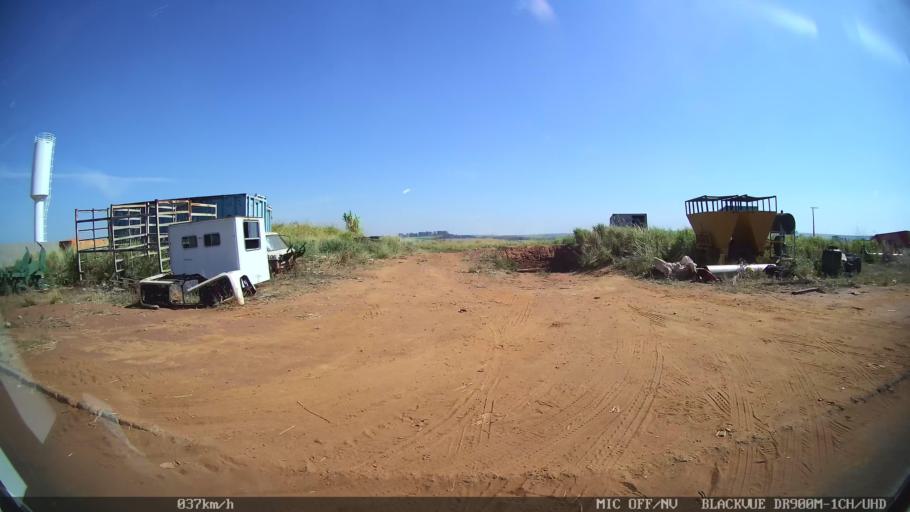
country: BR
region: Sao Paulo
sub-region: Batatais
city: Batatais
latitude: -20.8774
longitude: -47.6003
